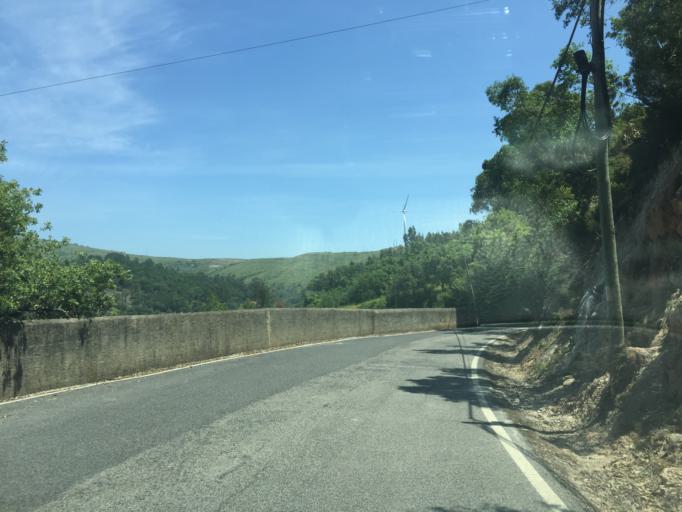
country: PT
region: Lisbon
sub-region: Mafra
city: Venda do Pinheiro
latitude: 38.8903
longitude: -9.2154
